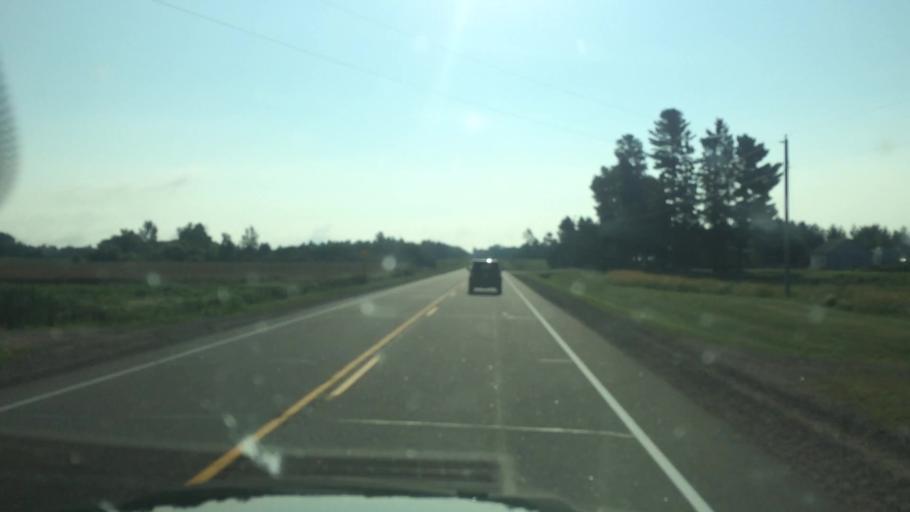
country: US
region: Wisconsin
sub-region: Langlade County
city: Antigo
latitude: 45.1400
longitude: -89.2275
